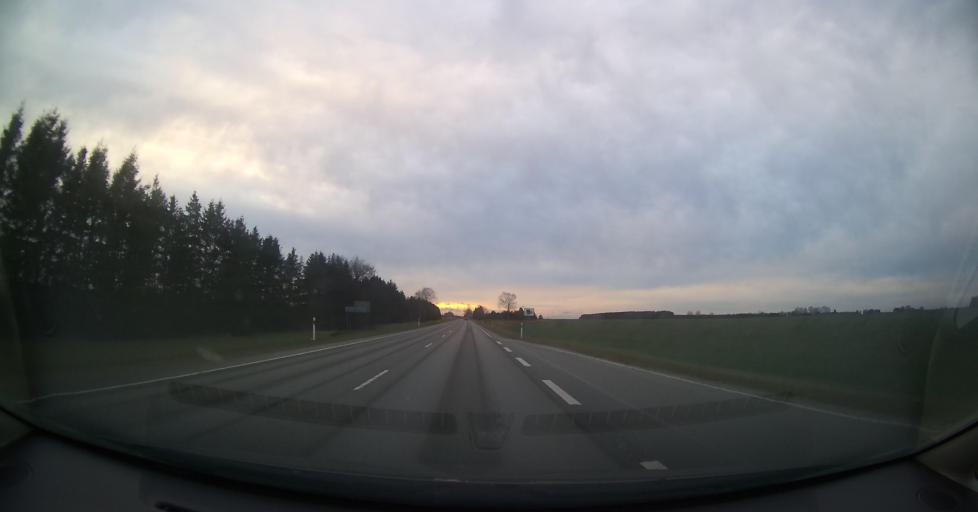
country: EE
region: Ida-Virumaa
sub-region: Kohtla-Nomme vald
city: Kohtla-Nomme
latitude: 59.4179
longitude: 27.1584
